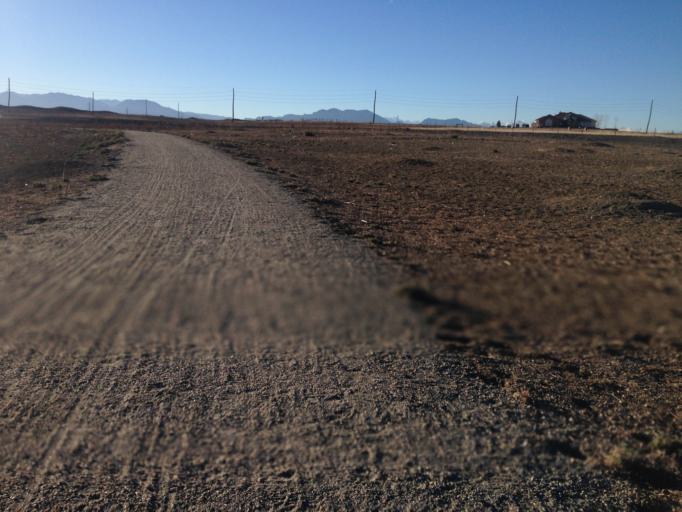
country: US
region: Colorado
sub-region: Broomfield County
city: Broomfield
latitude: 39.9358
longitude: -105.1161
